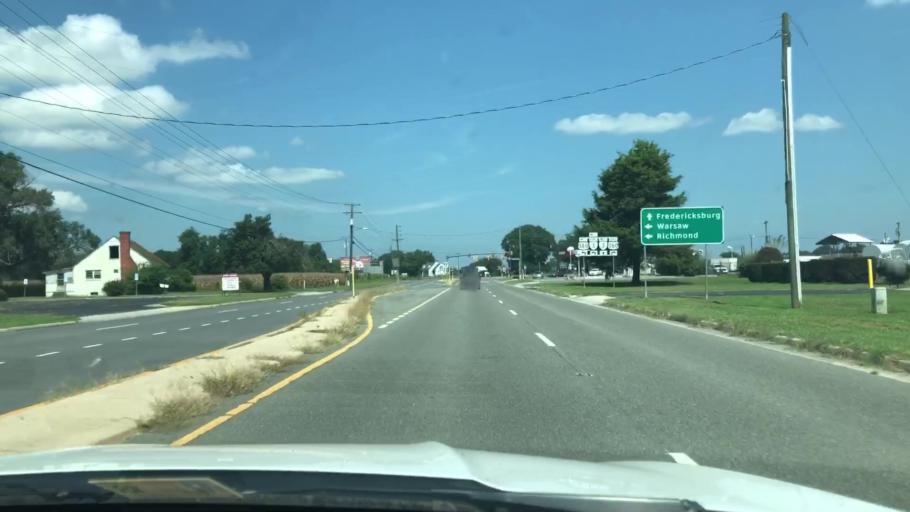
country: US
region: Virginia
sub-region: Richmond County
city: Warsaw
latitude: 37.9487
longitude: -76.7494
